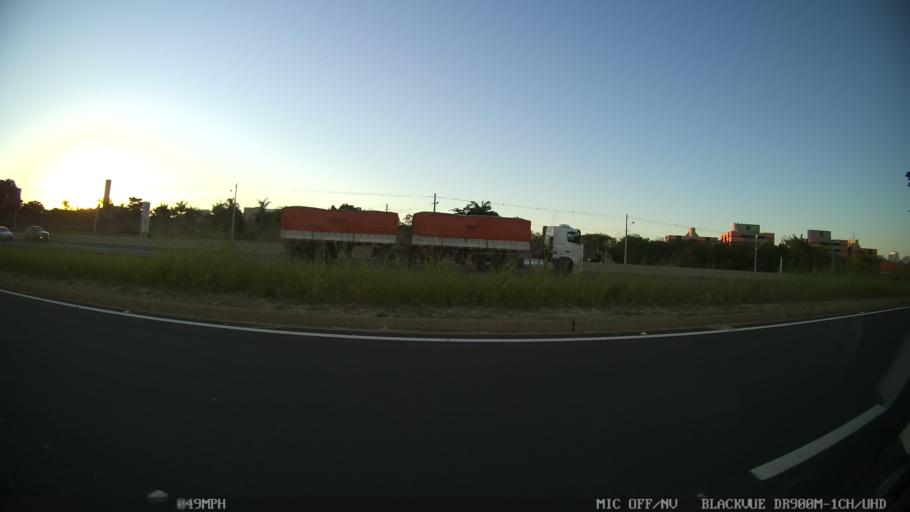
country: BR
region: Sao Paulo
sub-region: Sao Jose Do Rio Preto
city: Sao Jose do Rio Preto
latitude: -20.8516
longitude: -49.3970
